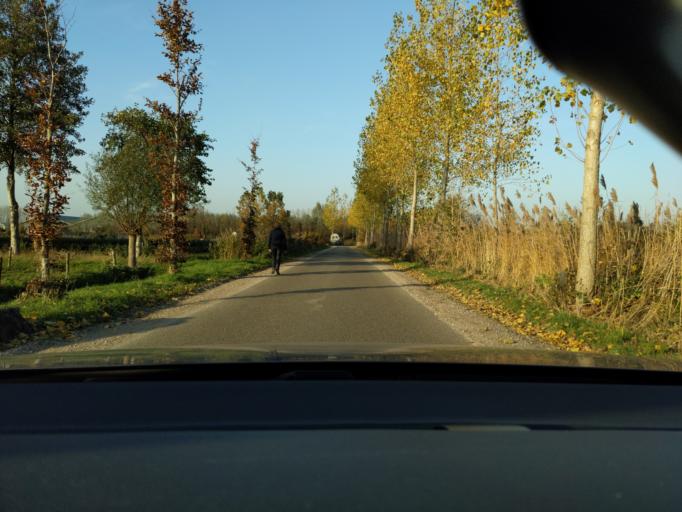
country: NL
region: North Brabant
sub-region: Gemeente Sint-Oedenrode
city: Sint-Oedenrode
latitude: 51.5589
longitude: 5.4252
